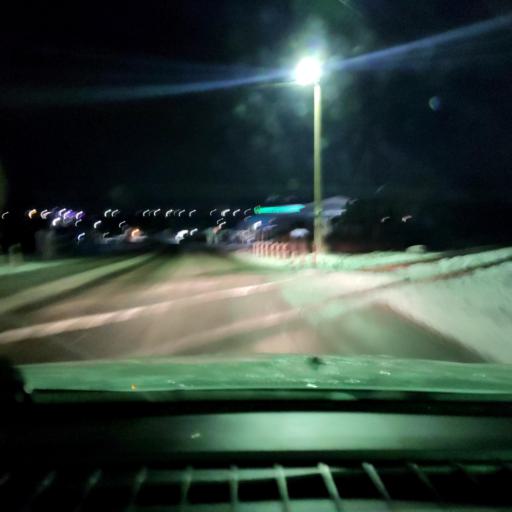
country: RU
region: Samara
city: Kurumoch
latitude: 53.4807
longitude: 50.0502
